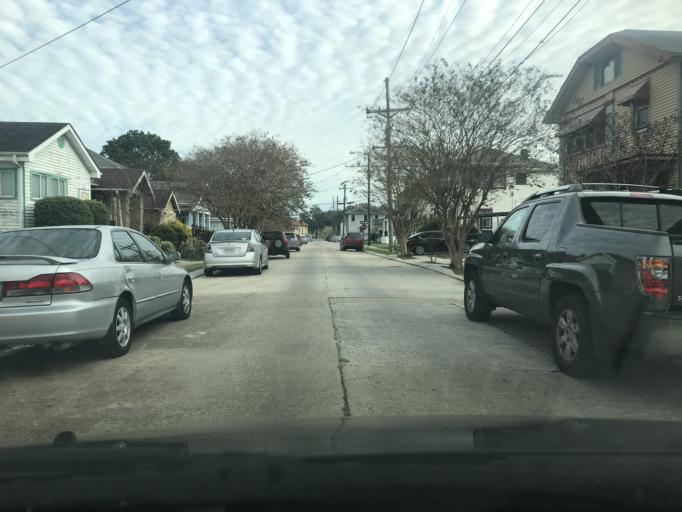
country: US
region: Louisiana
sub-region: Orleans Parish
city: New Orleans
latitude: 29.9516
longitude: -90.1032
